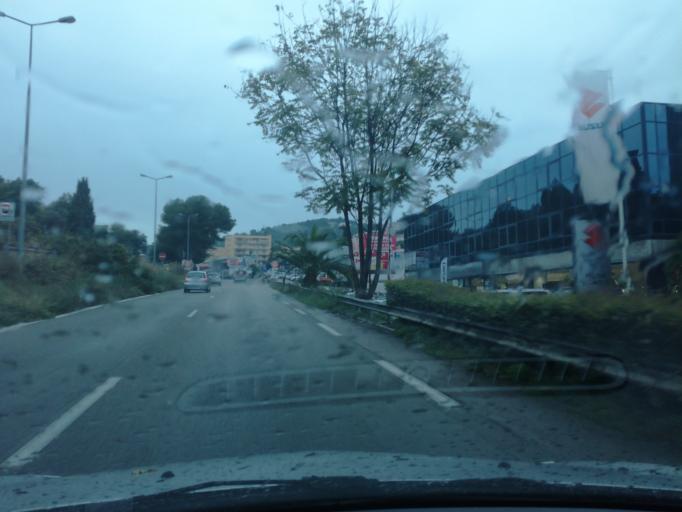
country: FR
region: Provence-Alpes-Cote d'Azur
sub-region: Departement des Alpes-Maritimes
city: Le Cannet
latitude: 43.5764
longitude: 7.0123
